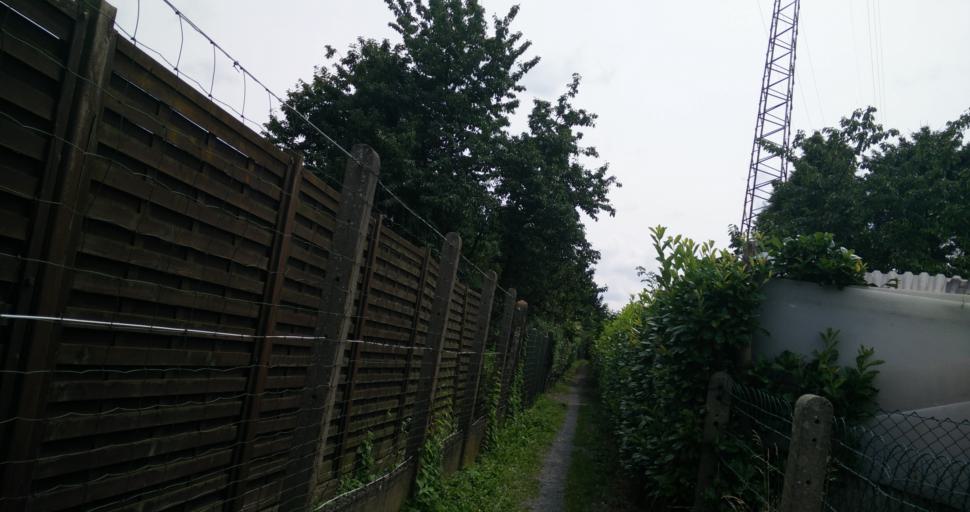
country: BE
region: Flanders
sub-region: Provincie Vlaams-Brabant
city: Halle
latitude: 50.7369
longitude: 4.2530
